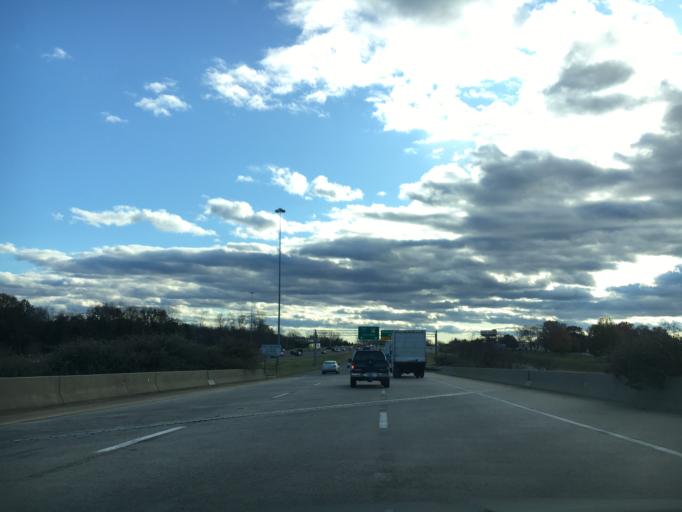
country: US
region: North Carolina
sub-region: Mecklenburg County
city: Pineville
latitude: 35.1229
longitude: -80.9201
